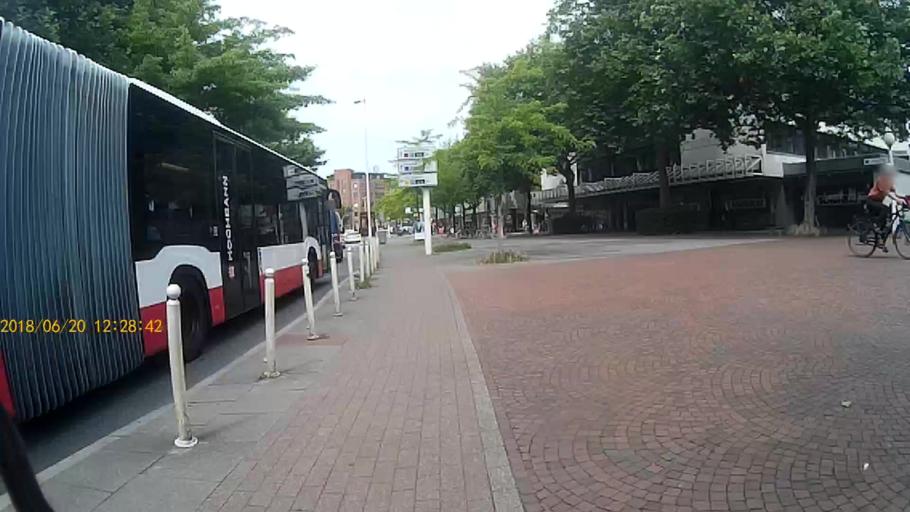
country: DE
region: Hamburg
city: Harburg
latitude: 53.4599
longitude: 9.9838
